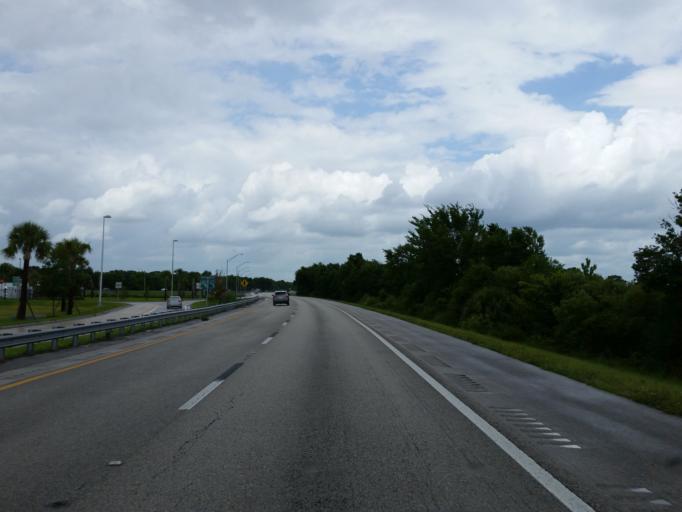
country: US
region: Florida
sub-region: Indian River County
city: Fellsmere
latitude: 27.6027
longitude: -80.8223
